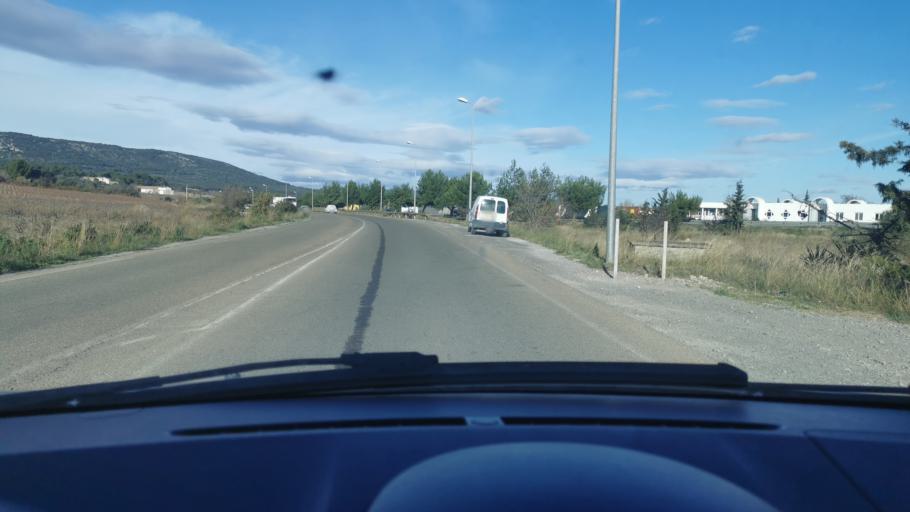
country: FR
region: Languedoc-Roussillon
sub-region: Departement de l'Herault
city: Frontignan
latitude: 43.4631
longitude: 3.7663
